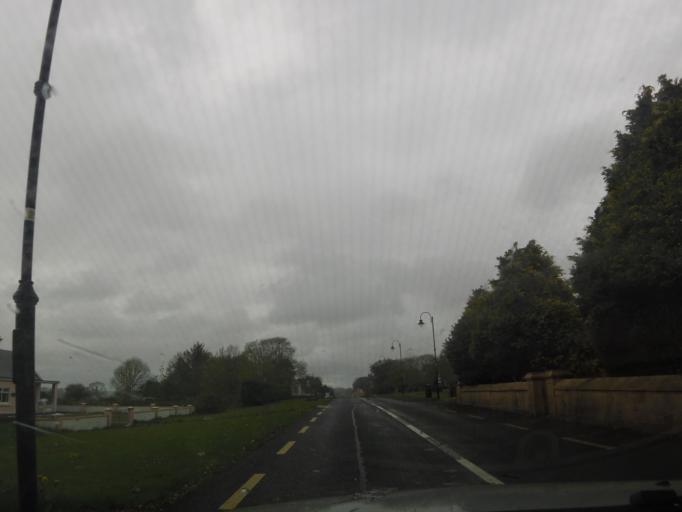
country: IE
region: Connaught
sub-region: Maigh Eo
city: Ballinrobe
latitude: 53.5707
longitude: -9.2314
